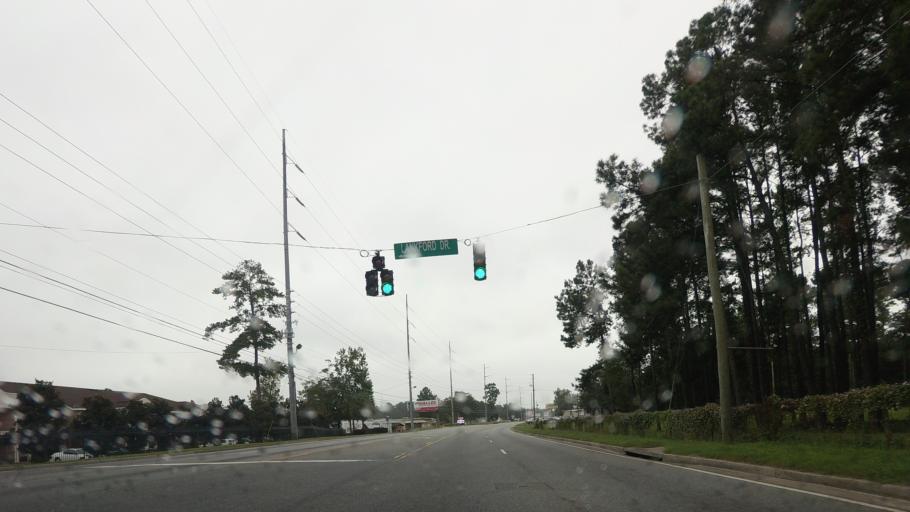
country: US
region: Georgia
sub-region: Lowndes County
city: Remerton
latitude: 30.8341
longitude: -83.3125
